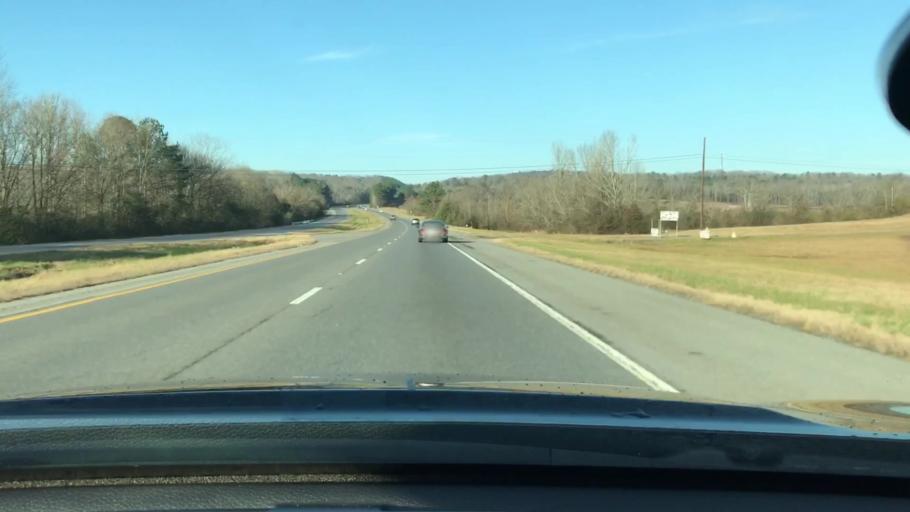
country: US
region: Alabama
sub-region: Shelby County
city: Harpersville
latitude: 33.3501
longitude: -86.4645
